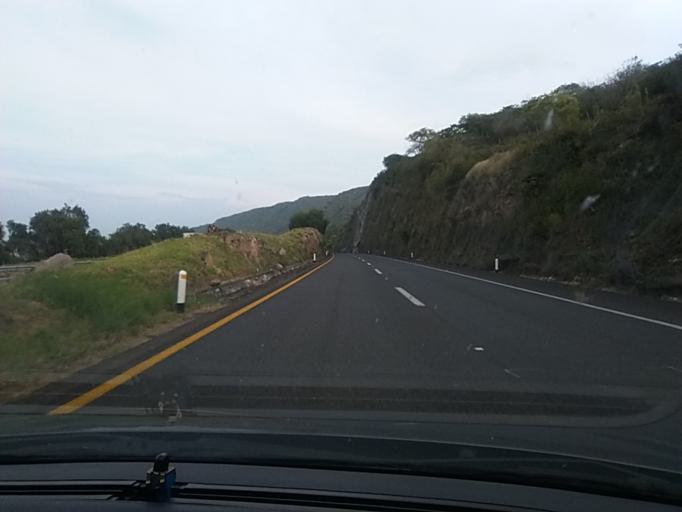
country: MX
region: Michoacan
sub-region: Cuitzeo
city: San Juan Benito Juarez (San Juan Tararameo)
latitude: 19.8995
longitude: -101.1175
